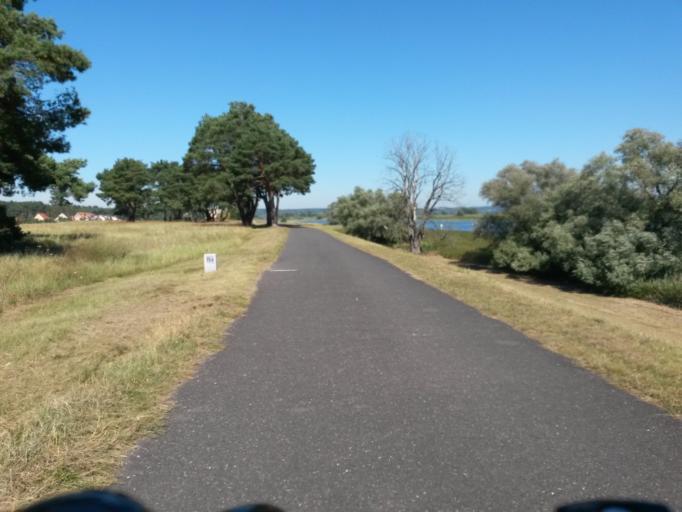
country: PL
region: West Pomeranian Voivodeship
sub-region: Powiat gryfinski
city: Cedynia
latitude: 52.8799
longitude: 14.1554
